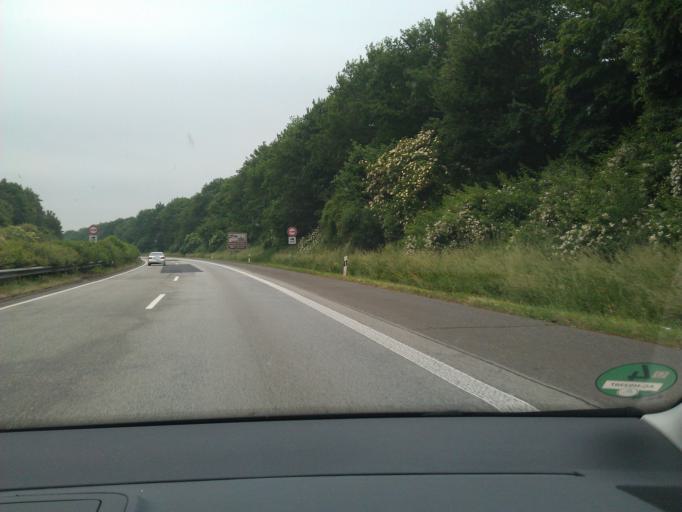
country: DE
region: Rheinland-Pfalz
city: Saffig
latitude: 50.3631
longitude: 7.4350
